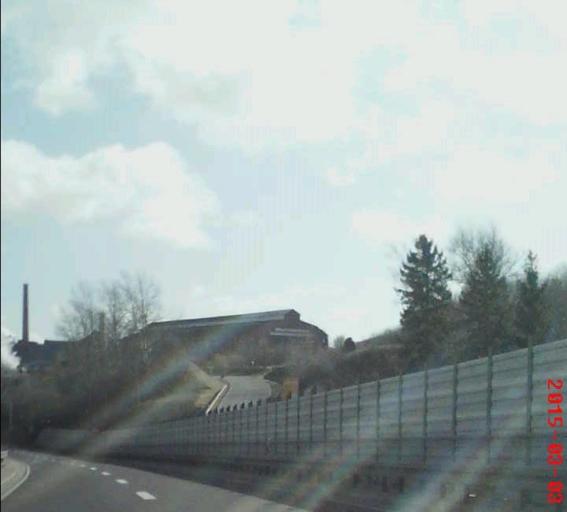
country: DE
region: Thuringia
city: Unterwellenborn
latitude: 50.6577
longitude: 11.4171
